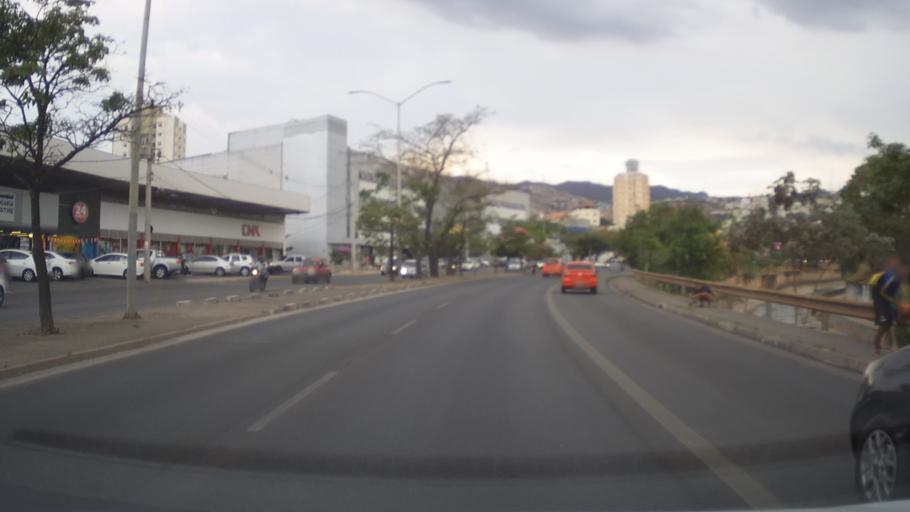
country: BR
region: Minas Gerais
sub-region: Belo Horizonte
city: Belo Horizonte
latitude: -19.9130
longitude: -43.9082
